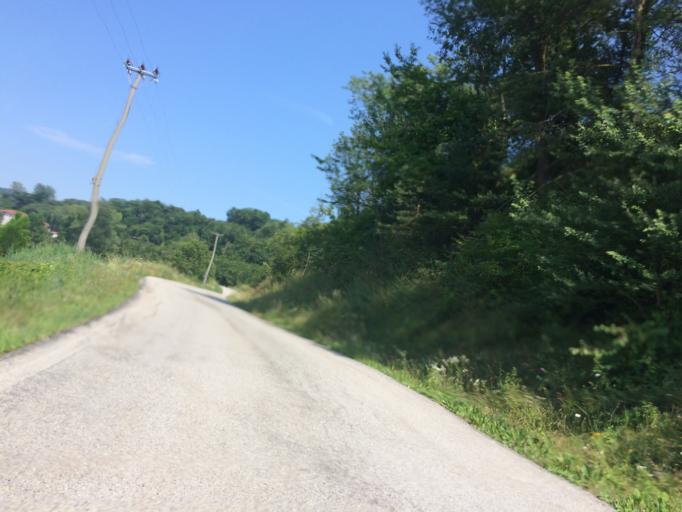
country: IT
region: Piedmont
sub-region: Provincia di Cuneo
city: Cravanzana
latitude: 44.5819
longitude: 8.1248
